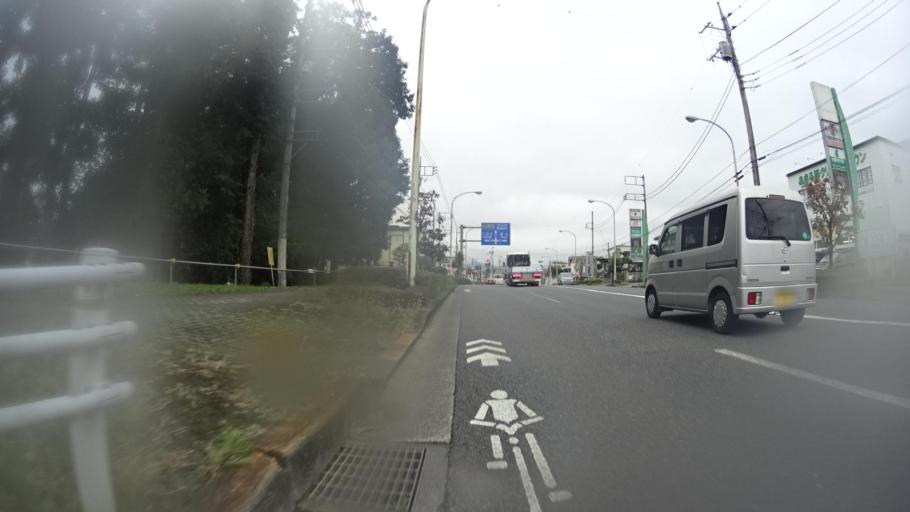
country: JP
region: Tokyo
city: Fussa
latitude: 35.7227
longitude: 139.2997
